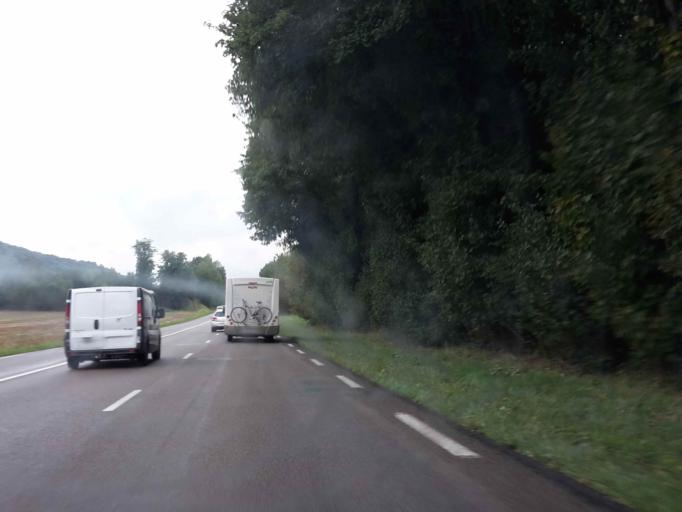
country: FR
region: Franche-Comte
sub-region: Departement du Doubs
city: Roulans
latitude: 47.3127
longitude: 6.2194
